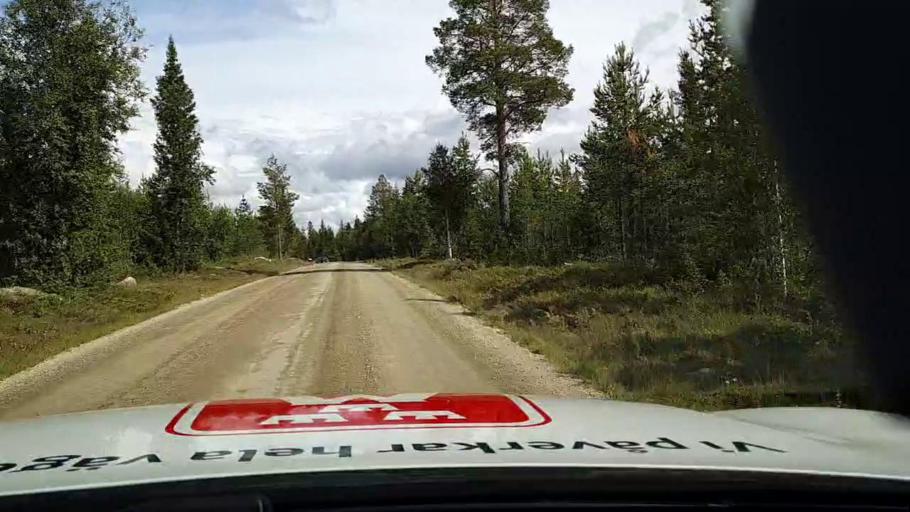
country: SE
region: Jaemtland
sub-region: Are Kommun
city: Jarpen
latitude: 62.5477
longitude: 13.4630
